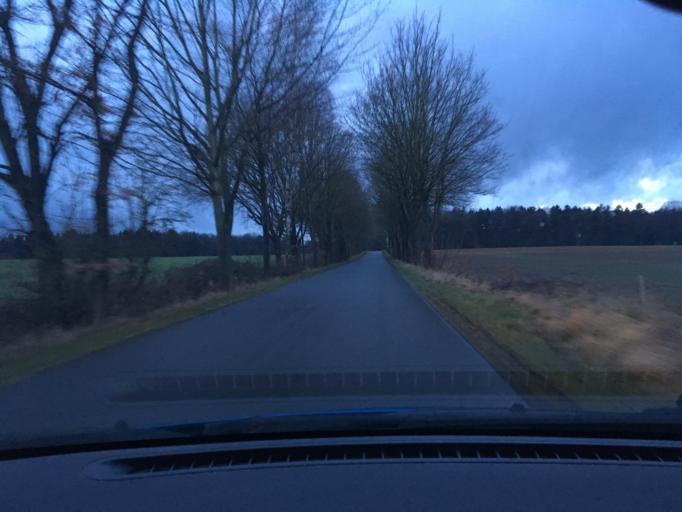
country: DE
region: Lower Saxony
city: Barnstedt
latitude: 53.1348
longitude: 10.3567
